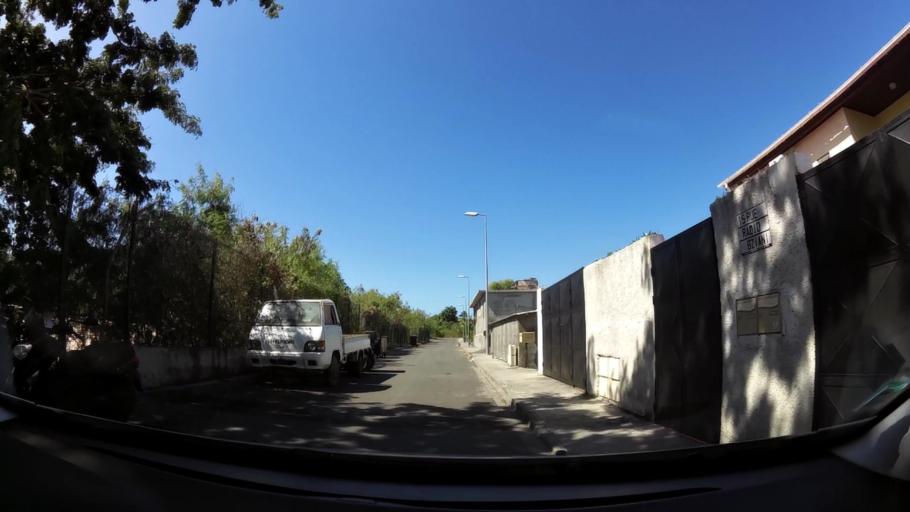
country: YT
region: Pamandzi
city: Pamandzi
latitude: -12.7976
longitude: 45.2800
